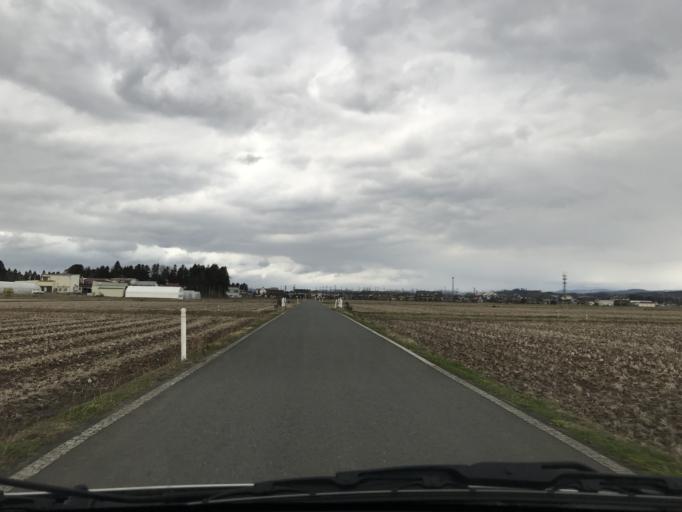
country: JP
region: Iwate
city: Mizusawa
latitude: 39.1094
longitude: 141.1641
